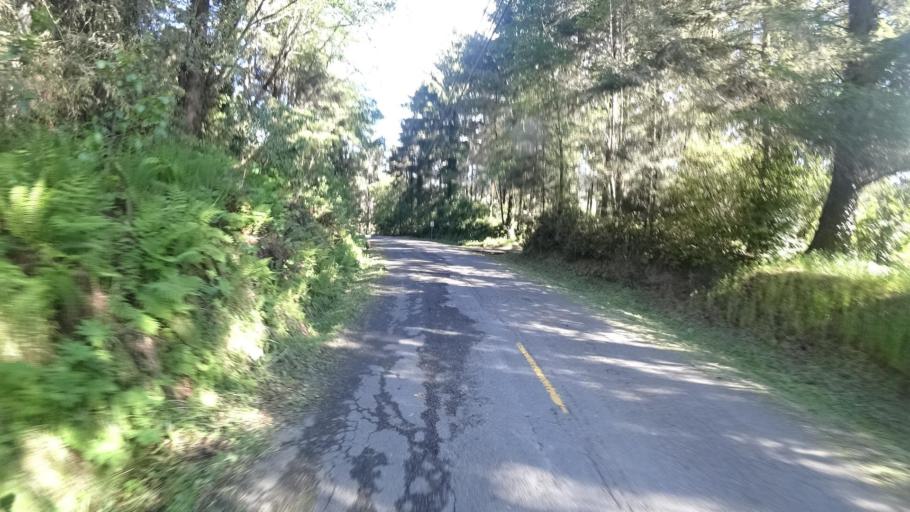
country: US
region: California
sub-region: Humboldt County
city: Westhaven-Moonstone
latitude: 41.0092
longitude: -124.1065
